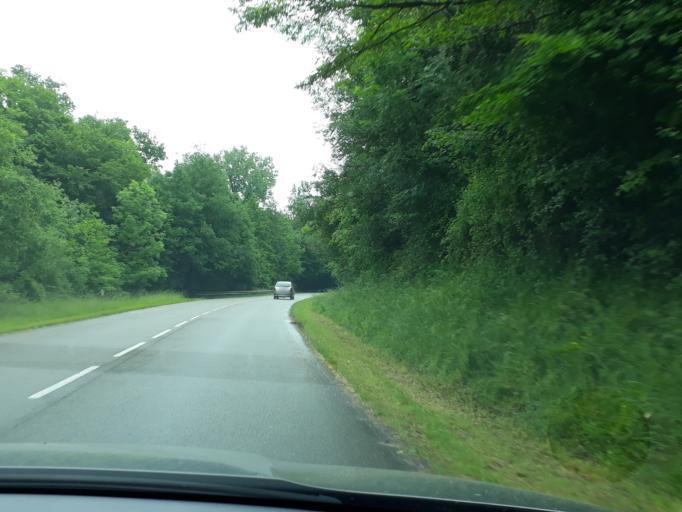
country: FR
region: Limousin
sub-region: Departement de la Correze
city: Cosnac
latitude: 45.1537
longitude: 1.6269
